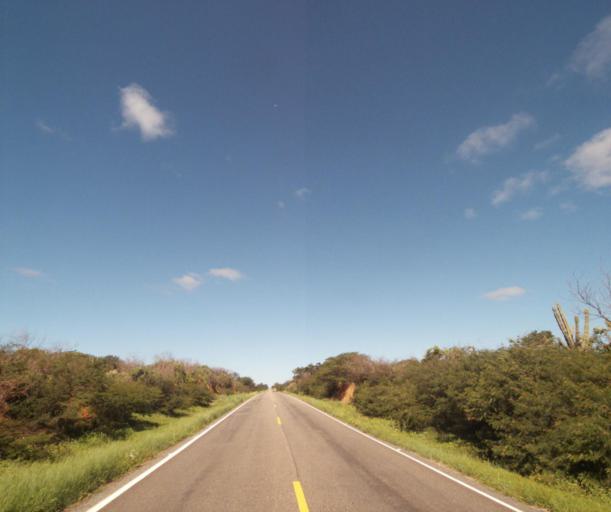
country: BR
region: Bahia
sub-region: Palmas De Monte Alto
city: Palmas de Monte Alto
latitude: -14.2443
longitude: -43.0982
